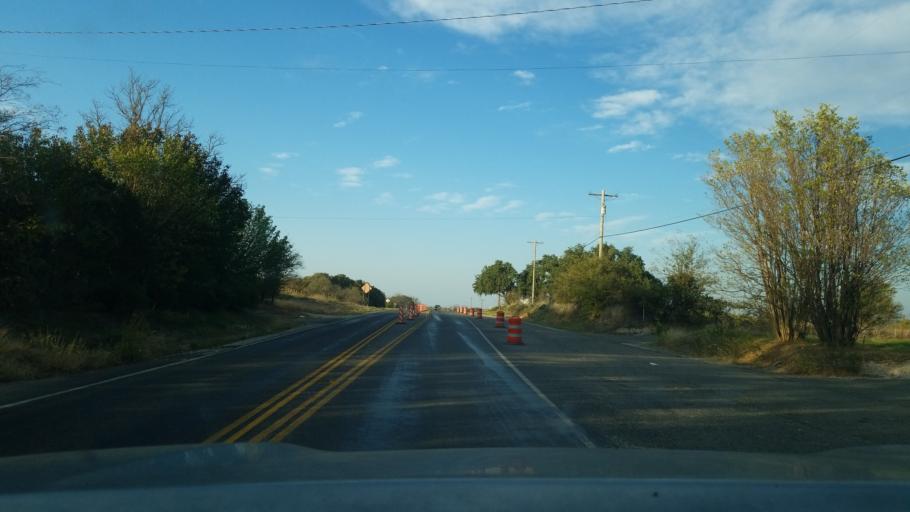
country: US
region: Texas
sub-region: Brown County
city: Lake Brownwood
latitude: 32.1087
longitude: -98.9643
